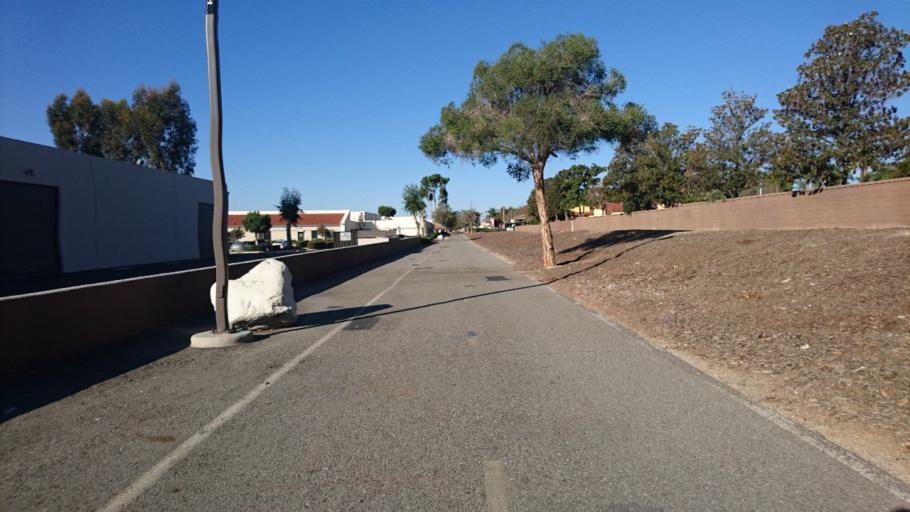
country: US
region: California
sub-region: San Bernardino County
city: Upland
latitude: 34.0978
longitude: -117.6681
